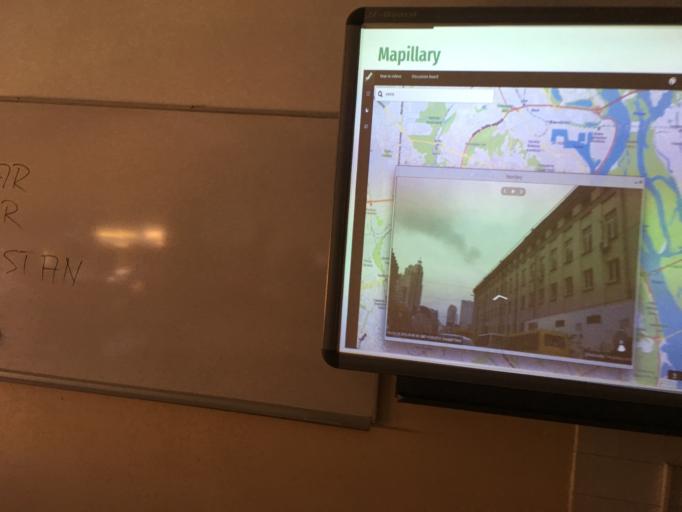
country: HR
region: Grad Zagreb
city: Novi Zagreb
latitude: 45.7731
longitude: 15.9823
